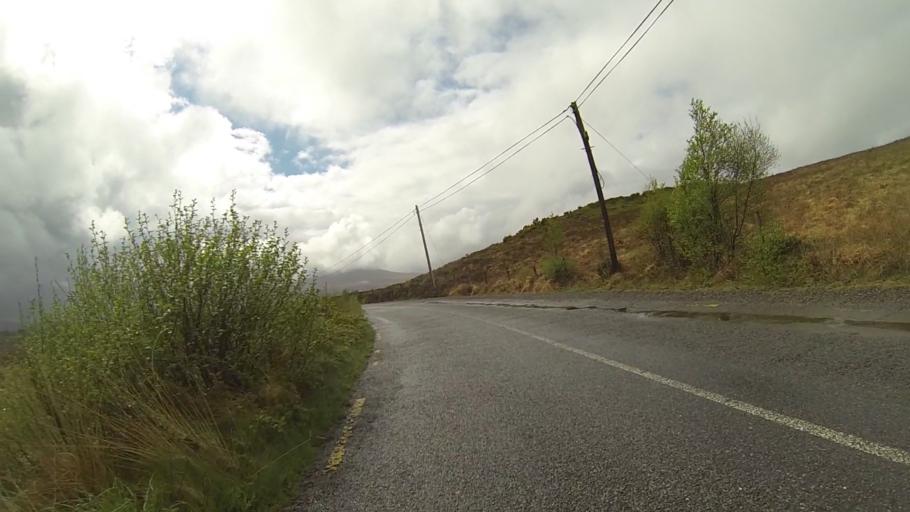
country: IE
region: Munster
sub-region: Ciarrai
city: Kenmare
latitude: 51.9022
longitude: -9.7442
